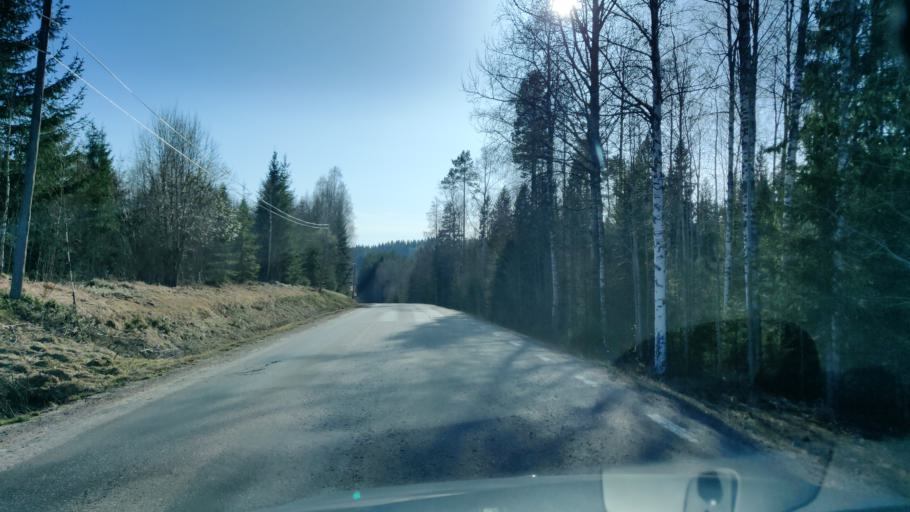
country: SE
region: Vaermland
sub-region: Sunne Kommun
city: Sunne
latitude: 59.9929
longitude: 13.2829
